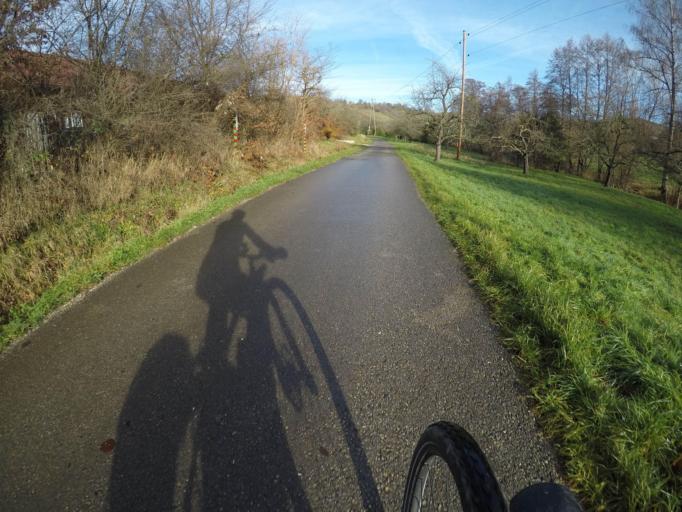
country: DE
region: Baden-Wuerttemberg
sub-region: Tuebingen Region
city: Metzingen
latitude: 48.5389
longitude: 9.3038
